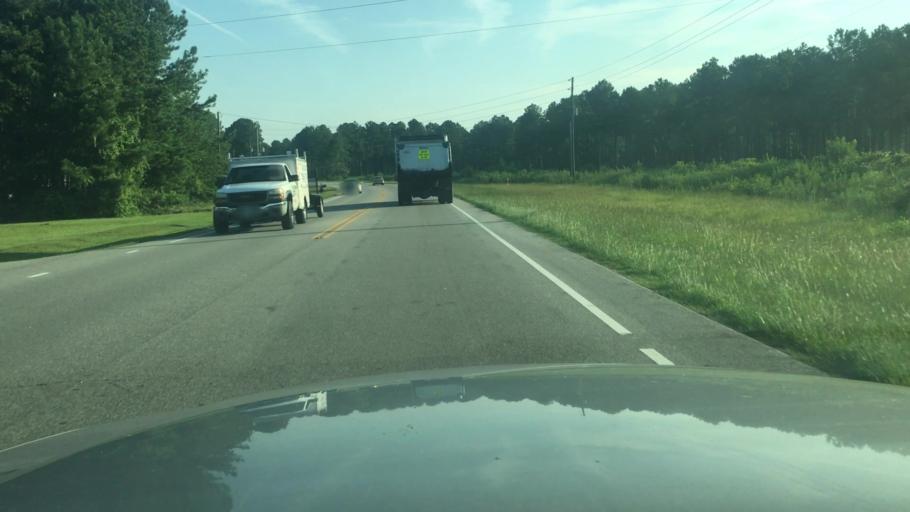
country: US
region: North Carolina
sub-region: Harnett County
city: Walkertown
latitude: 35.1929
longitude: -78.8500
